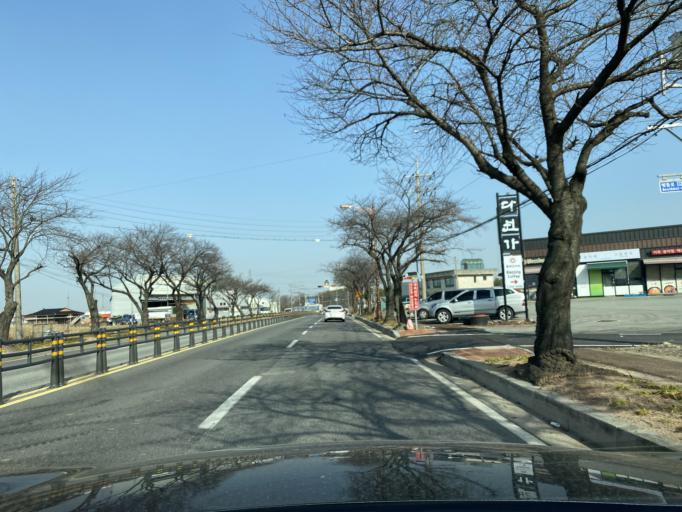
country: KR
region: Chungcheongnam-do
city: Yesan
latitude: 36.7096
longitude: 126.8403
